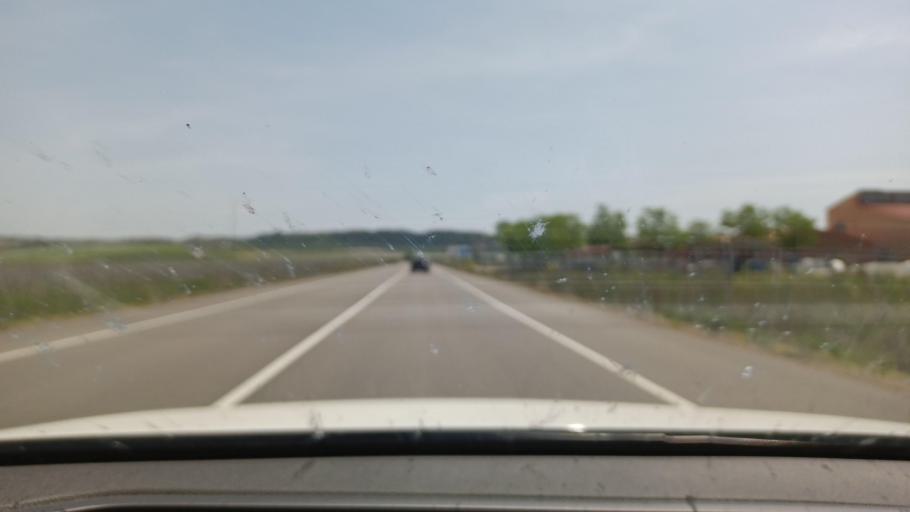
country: ES
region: Castille and Leon
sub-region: Provincia de Valladolid
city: Portillo
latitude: 41.4918
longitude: -4.6140
